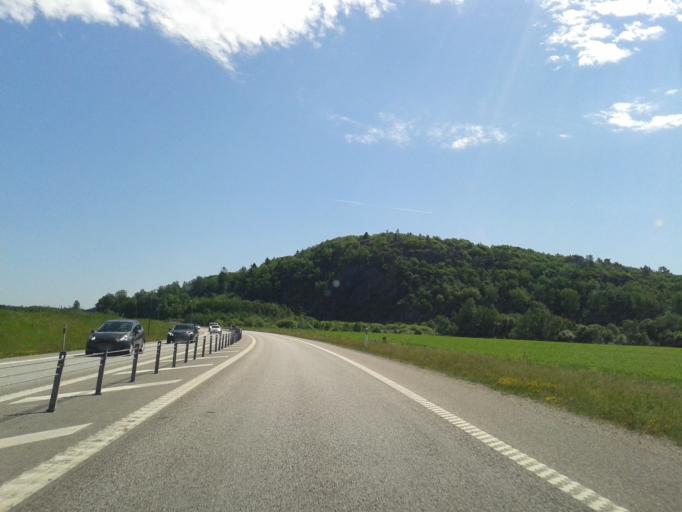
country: SE
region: Vaestra Goetaland
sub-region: Orust
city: Henan
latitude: 58.3465
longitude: 11.7524
